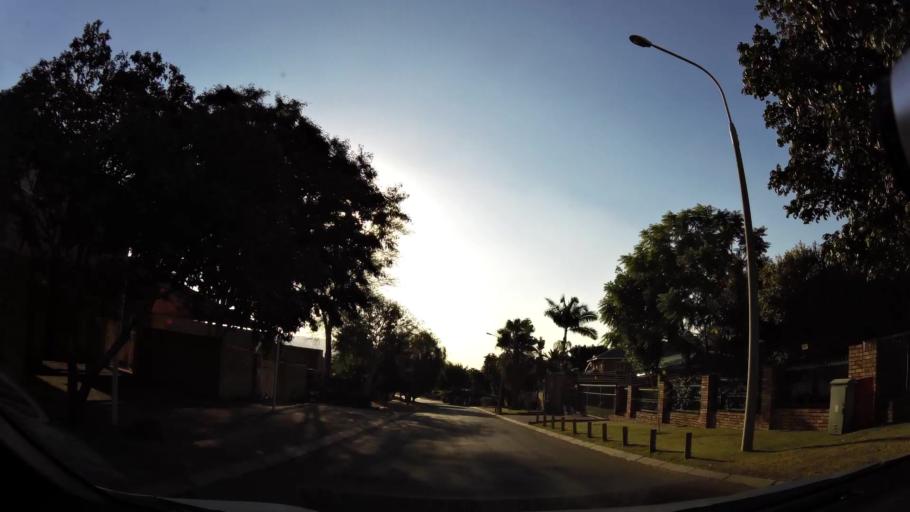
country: ZA
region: North-West
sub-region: Bojanala Platinum District Municipality
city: Rustenburg
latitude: -25.6834
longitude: 27.2382
